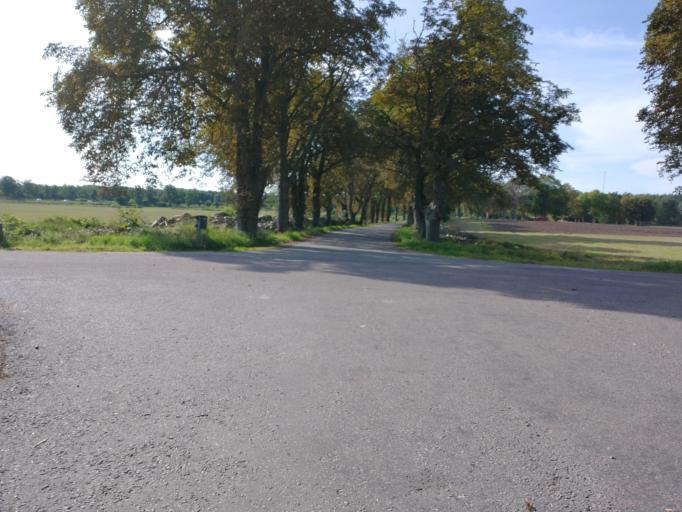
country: SE
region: Kalmar
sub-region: Kalmar Kommun
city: Lindsdal
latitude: 56.7769
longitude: 16.3244
